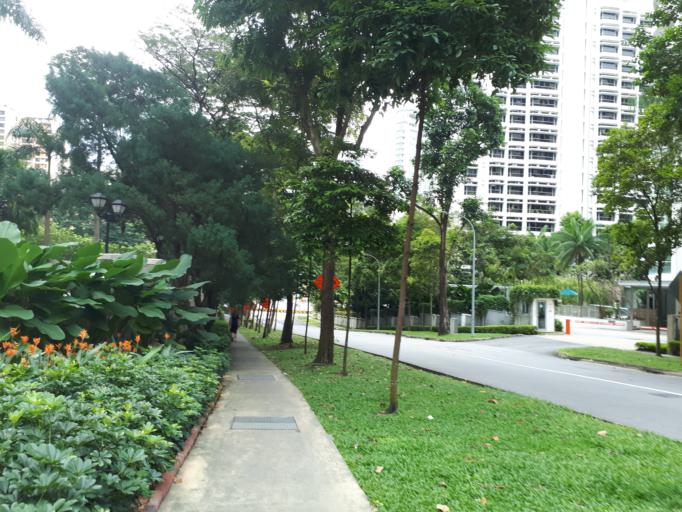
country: SG
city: Singapore
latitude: 1.2976
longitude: 103.8337
